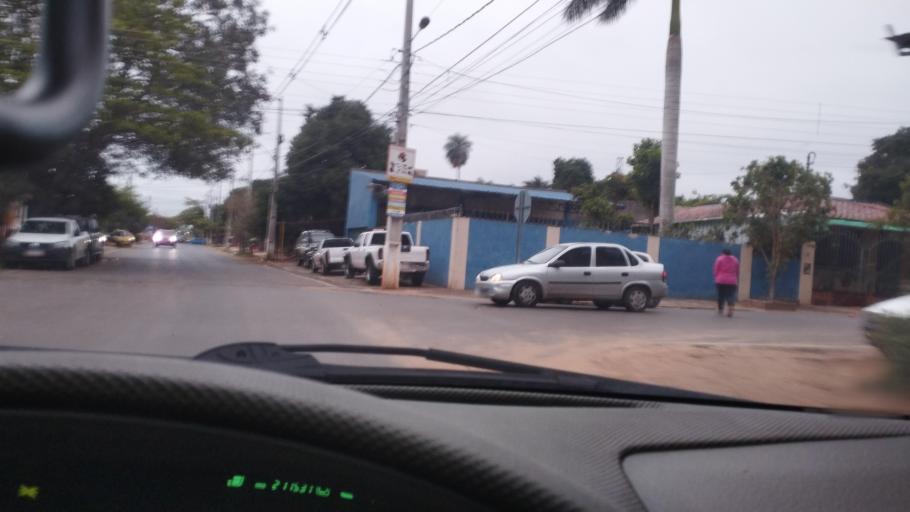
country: PY
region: Central
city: Fernando de la Mora
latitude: -25.3034
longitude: -57.5304
